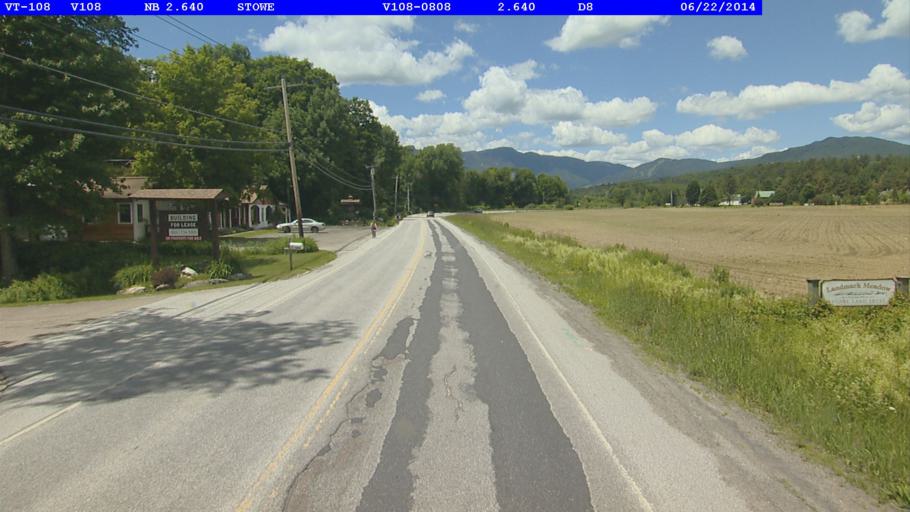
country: US
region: Vermont
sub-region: Lamoille County
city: Morristown
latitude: 44.4800
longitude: -72.7250
